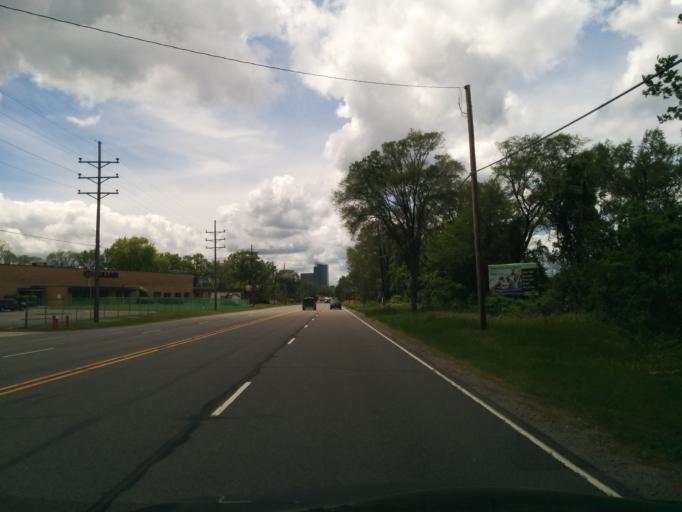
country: US
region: Indiana
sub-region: LaPorte County
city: Michigan City
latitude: 41.7248
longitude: -86.8780
